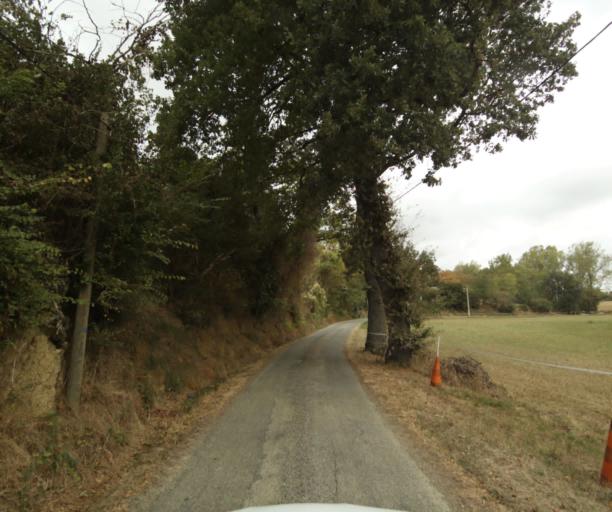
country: FR
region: Midi-Pyrenees
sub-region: Departement de la Haute-Garonne
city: Villefranche-de-Lauragais
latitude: 43.4106
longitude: 1.7172
